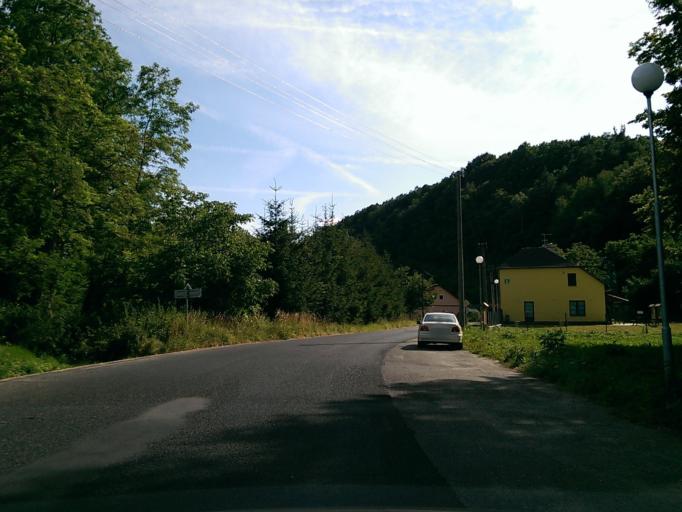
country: CZ
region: Central Bohemia
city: Bakov nad Jizerou
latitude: 50.4674
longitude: 14.9173
